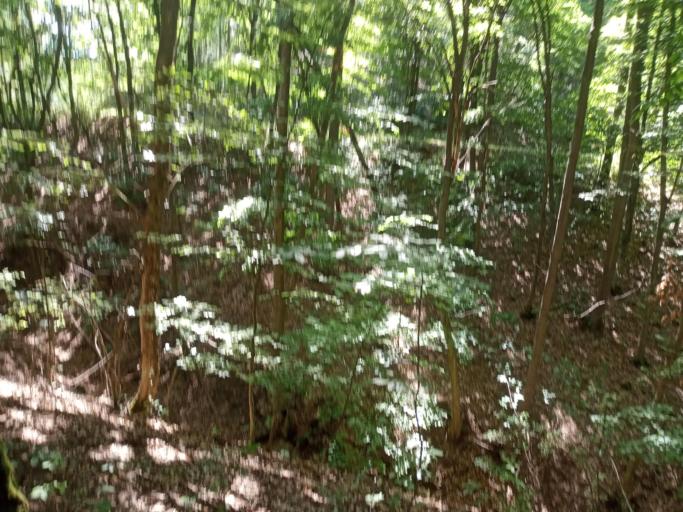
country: HU
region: Nograd
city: Matraverebely
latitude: 48.0069
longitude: 19.7609
